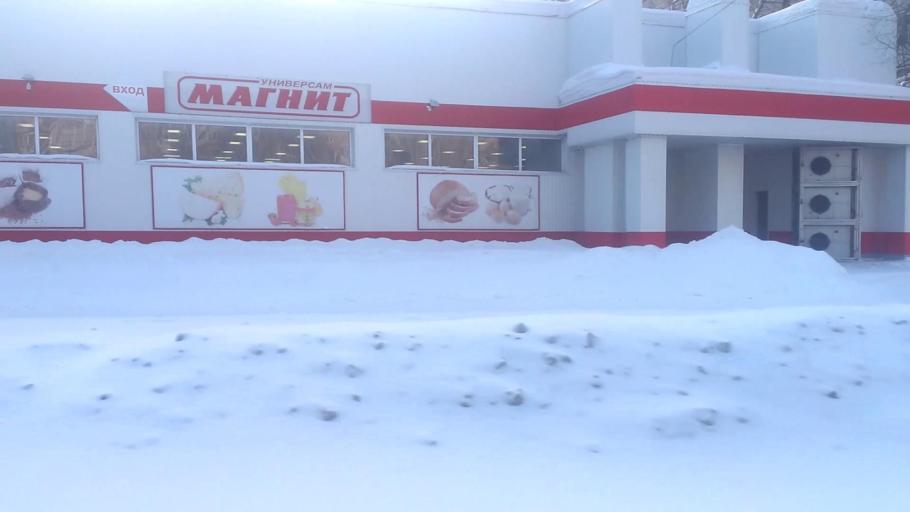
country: RU
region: Altai Krai
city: Novosilikatnyy
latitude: 53.3743
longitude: 83.6660
